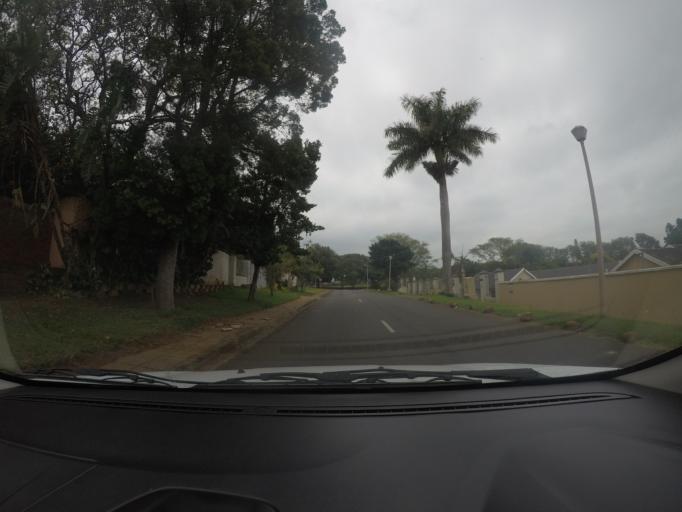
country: ZA
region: KwaZulu-Natal
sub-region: uThungulu District Municipality
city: Empangeni
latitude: -28.7532
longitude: 31.8869
